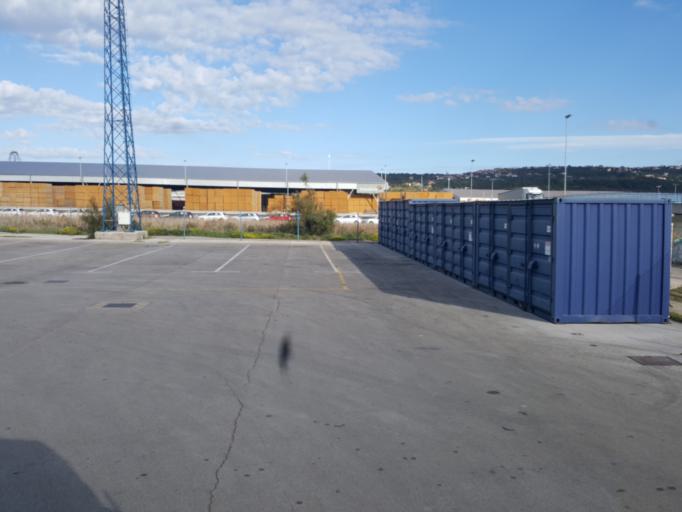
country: SI
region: Koper-Capodistria
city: Koper
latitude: 45.5577
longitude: 13.7478
